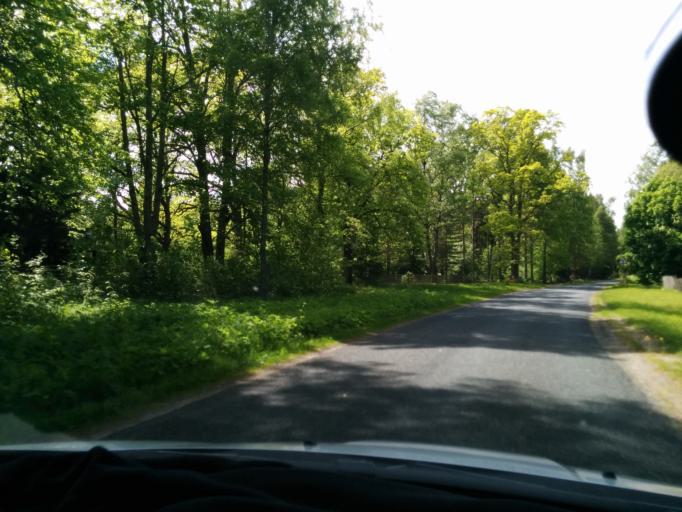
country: EE
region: Harju
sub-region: Loksa linn
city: Loksa
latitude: 59.5637
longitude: 25.6556
